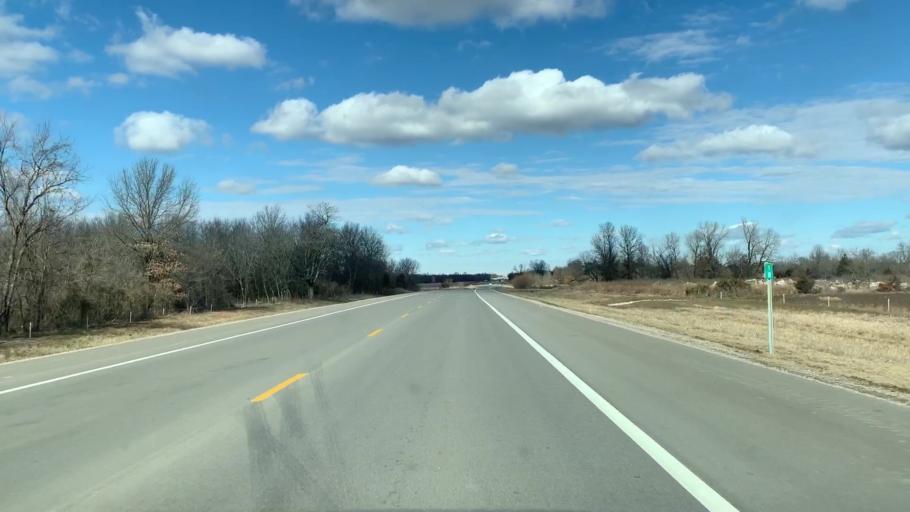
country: US
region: Kansas
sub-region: Cherokee County
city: Columbus
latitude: 37.2599
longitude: -94.8319
